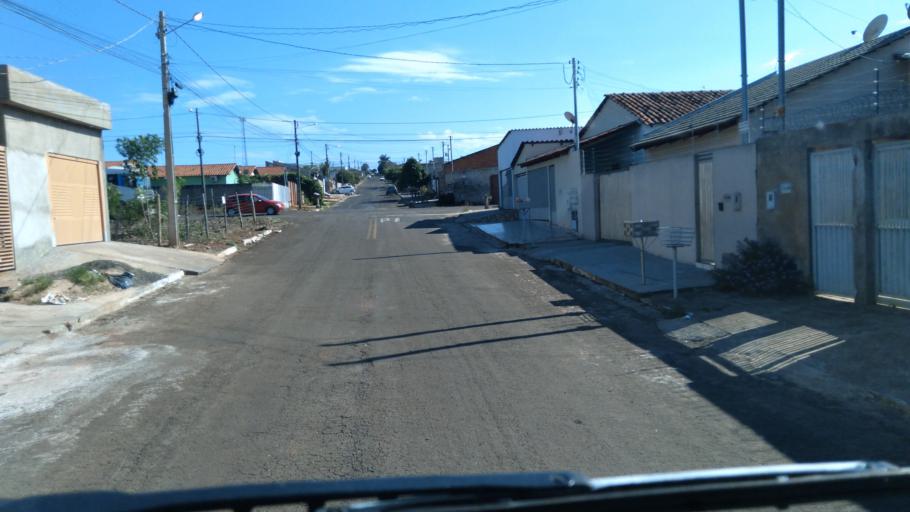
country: BR
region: Goias
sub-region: Mineiros
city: Mineiros
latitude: -17.5742
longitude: -52.5727
